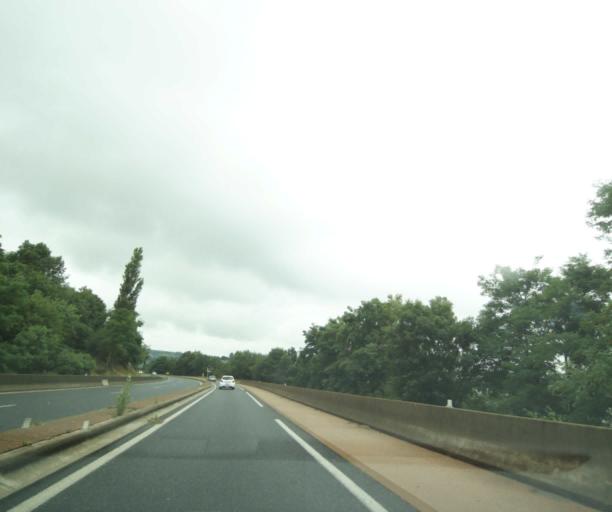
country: FR
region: Midi-Pyrenees
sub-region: Departement de l'Aveyron
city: Olemps
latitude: 44.3402
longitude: 2.5616
